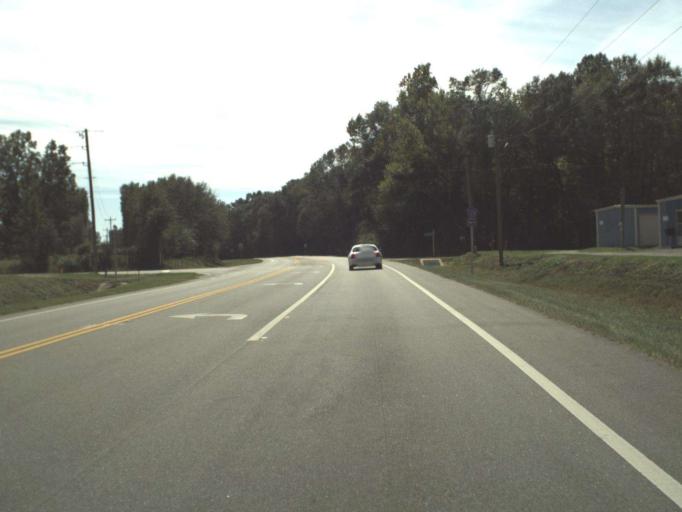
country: US
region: Florida
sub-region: Washington County
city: Chipley
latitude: 30.7364
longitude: -85.5550
